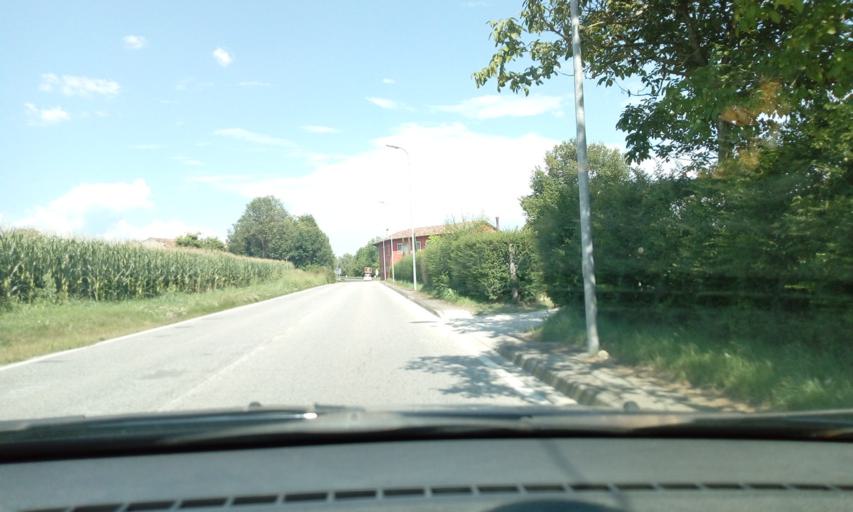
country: IT
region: Friuli Venezia Giulia
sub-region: Provincia di Udine
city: Pradamano
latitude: 46.0406
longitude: 13.3066
